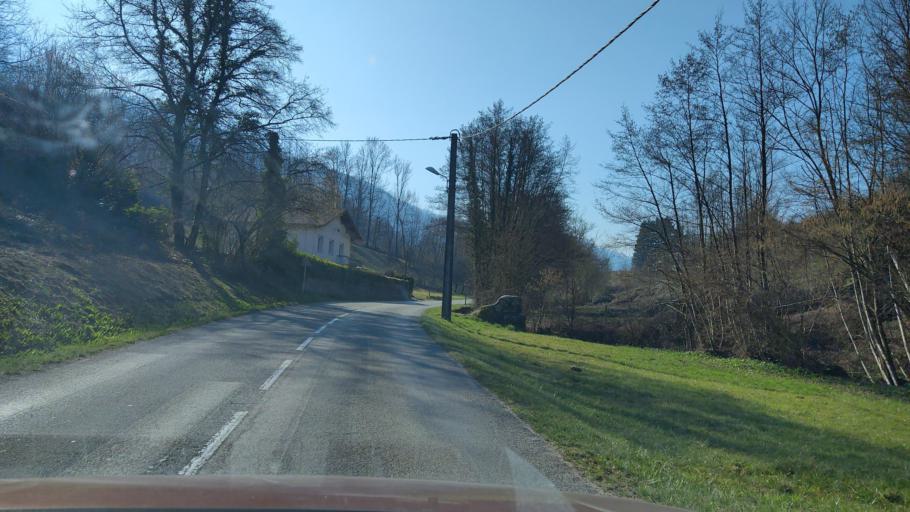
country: FR
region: Rhone-Alpes
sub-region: Departement de la Savoie
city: La Bridoire
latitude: 45.5216
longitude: 5.7394
